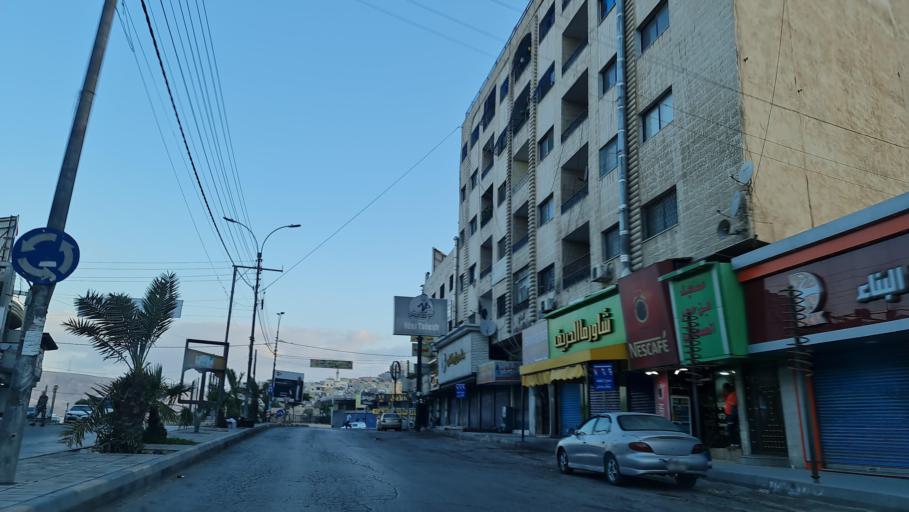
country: JO
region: Zarqa
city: Zarqa
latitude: 32.0777
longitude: 36.0754
